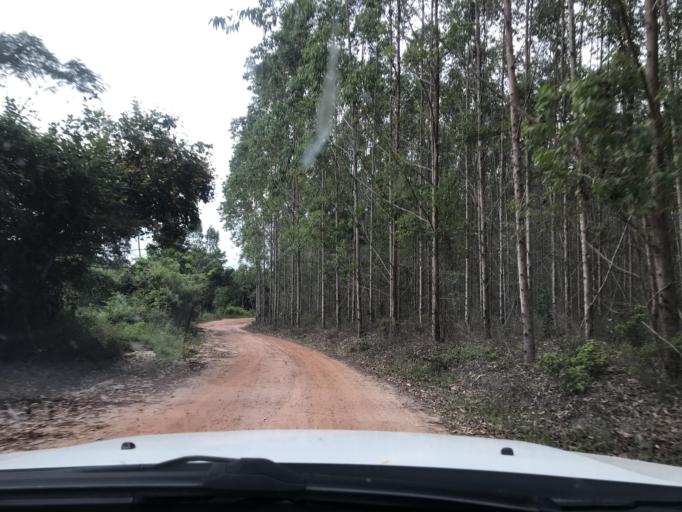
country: BR
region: Bahia
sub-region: Entre Rios
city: Entre Rios
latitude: -12.0988
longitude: -38.1897
